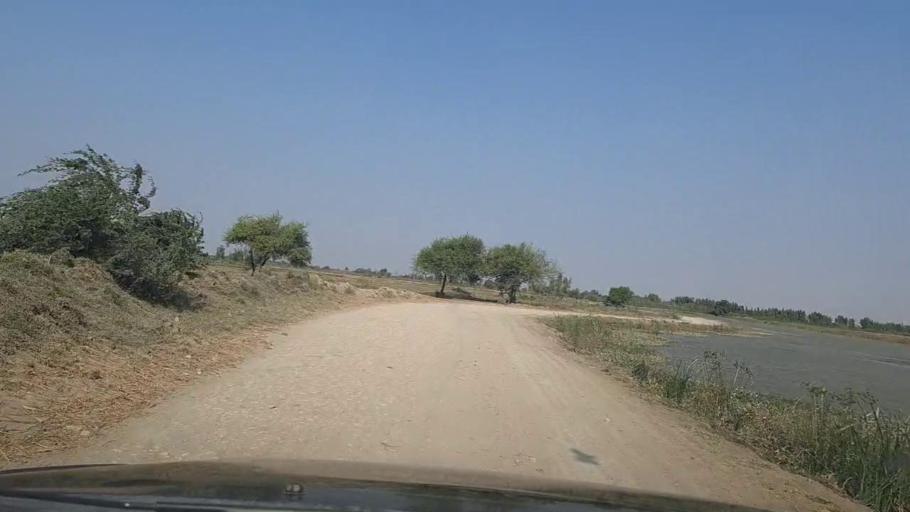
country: PK
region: Sindh
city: Thatta
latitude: 24.6266
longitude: 67.8137
